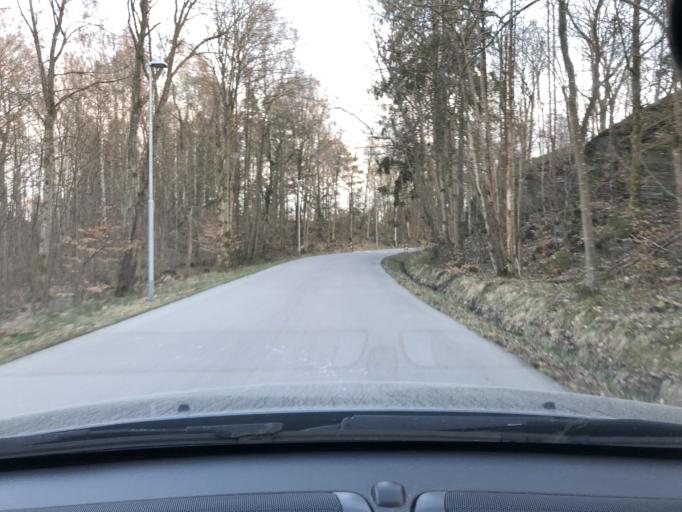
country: SE
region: Vaestra Goetaland
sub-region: Molndal
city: Moelndal
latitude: 57.6942
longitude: 12.0341
